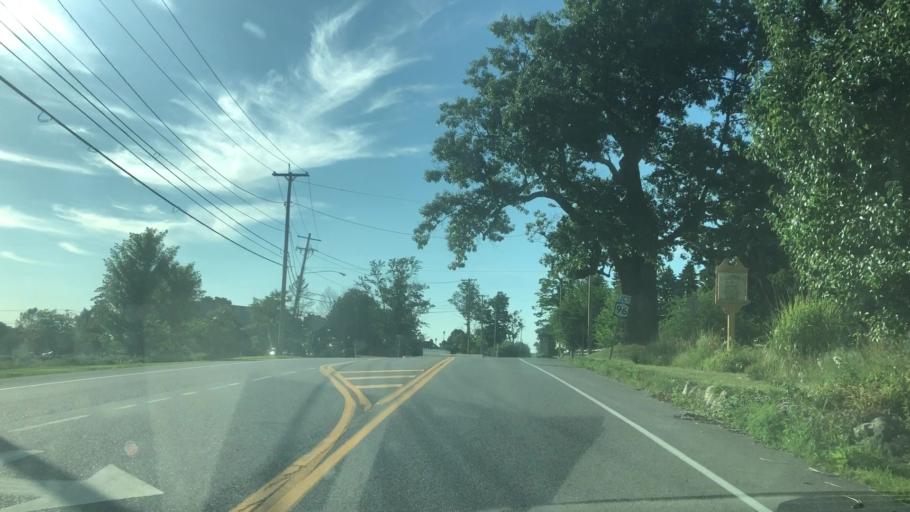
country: US
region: New York
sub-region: Ontario County
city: Victor
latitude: 43.0254
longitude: -77.4362
